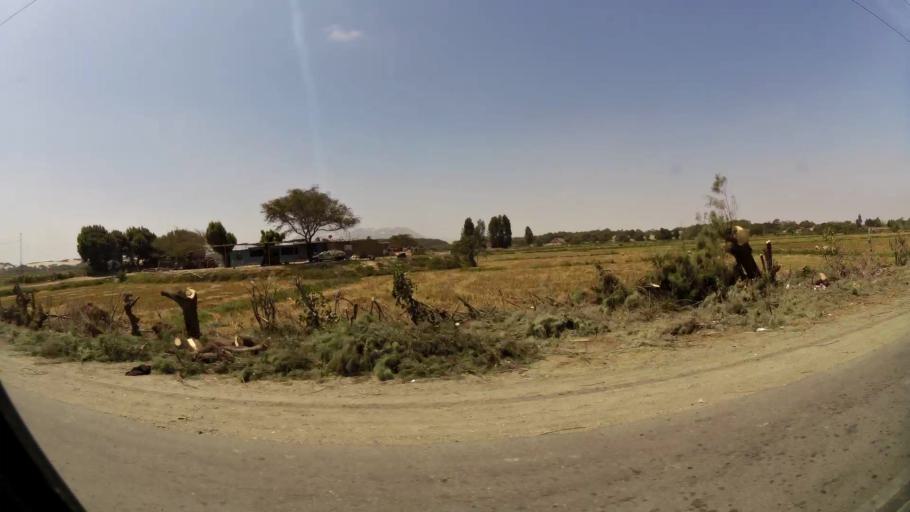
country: PE
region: La Libertad
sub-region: Provincia de Pacasmayo
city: San Pedro de Lloc
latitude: -7.4265
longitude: -79.4982
